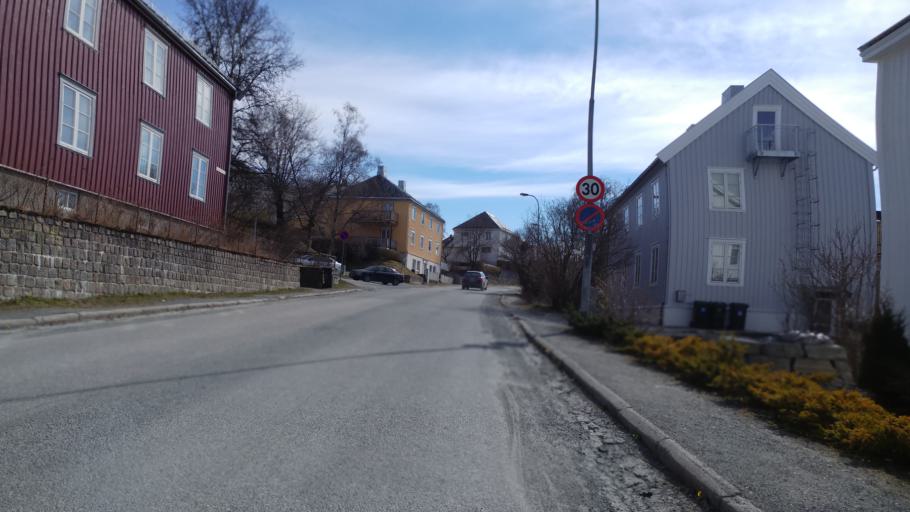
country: NO
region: Sor-Trondelag
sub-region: Trondheim
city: Trondheim
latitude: 63.4287
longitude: 10.4244
